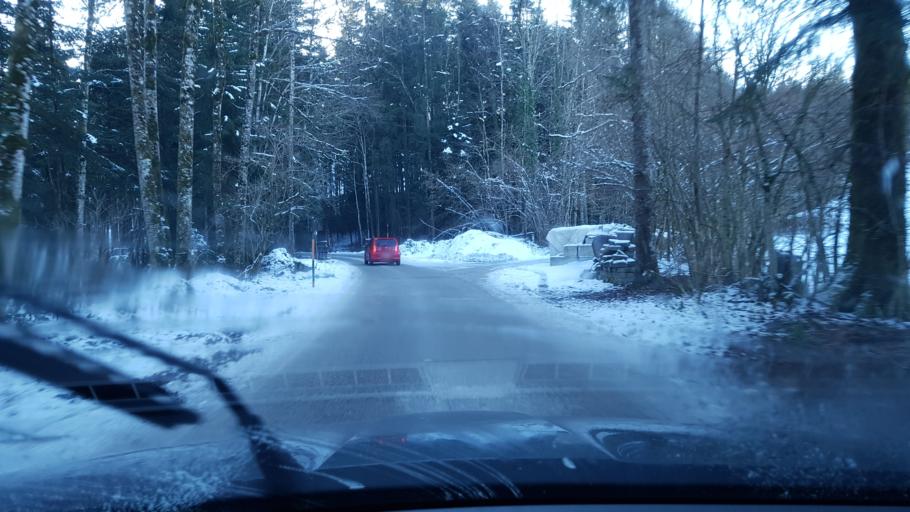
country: AT
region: Salzburg
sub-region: Politischer Bezirk Hallein
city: Scheffau am Tennengebirge
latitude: 47.6479
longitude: 13.2181
